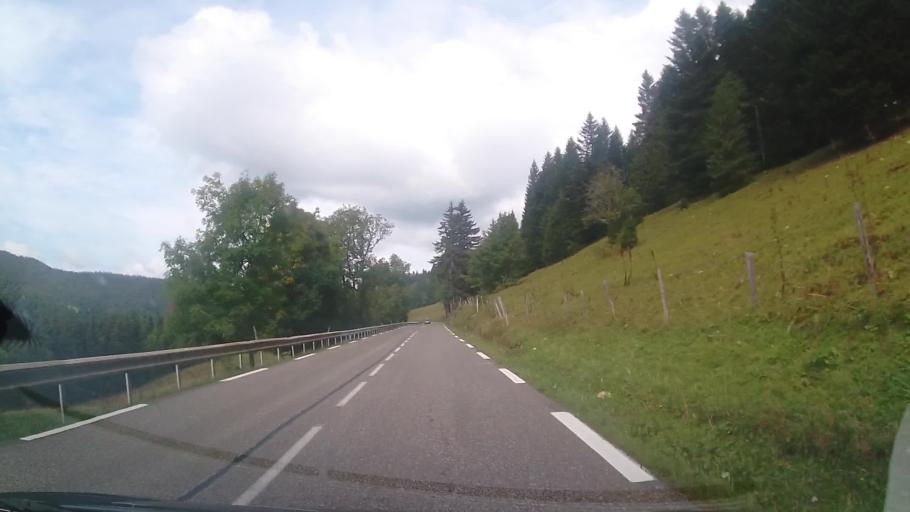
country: FR
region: Rhone-Alpes
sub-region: Departement de l'Ain
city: Gex
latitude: 46.3981
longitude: 6.0495
